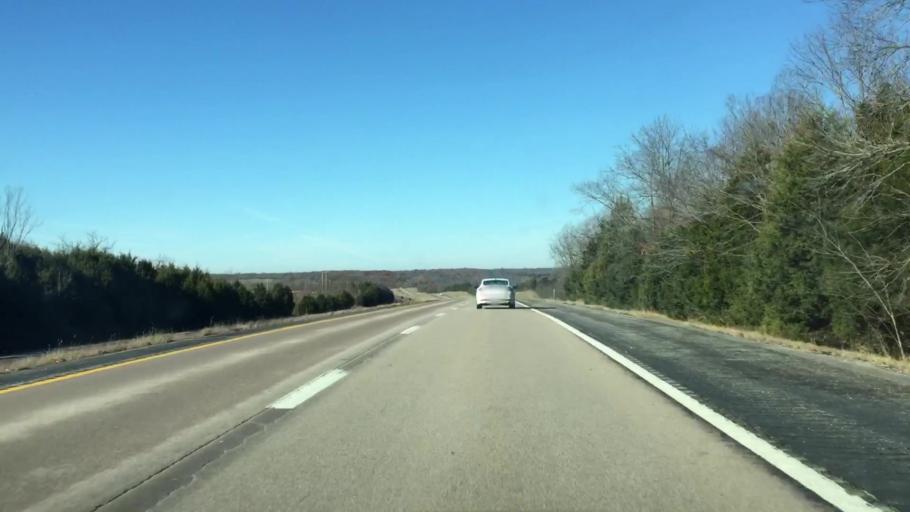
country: US
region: Missouri
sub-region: Miller County
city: Tuscumbia
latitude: 38.3736
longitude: -92.4289
